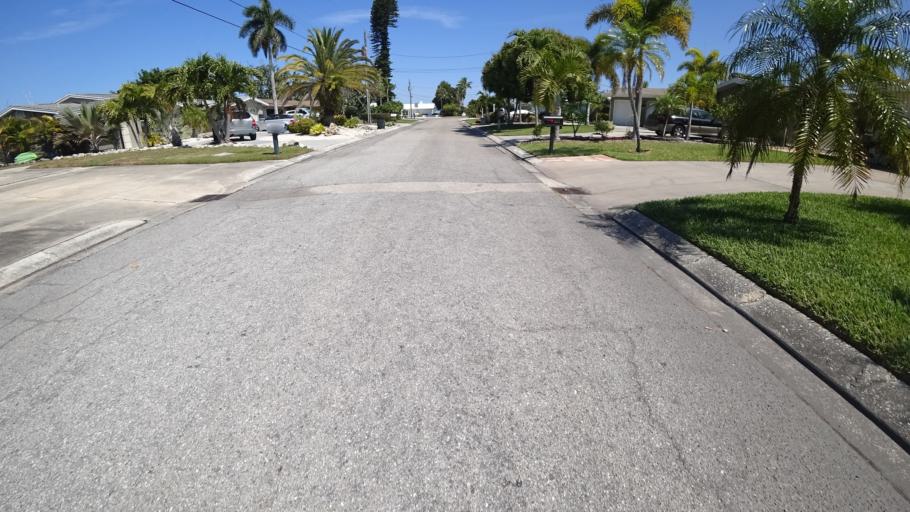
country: US
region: Florida
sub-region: Manatee County
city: Cortez
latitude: 27.4677
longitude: -82.6639
